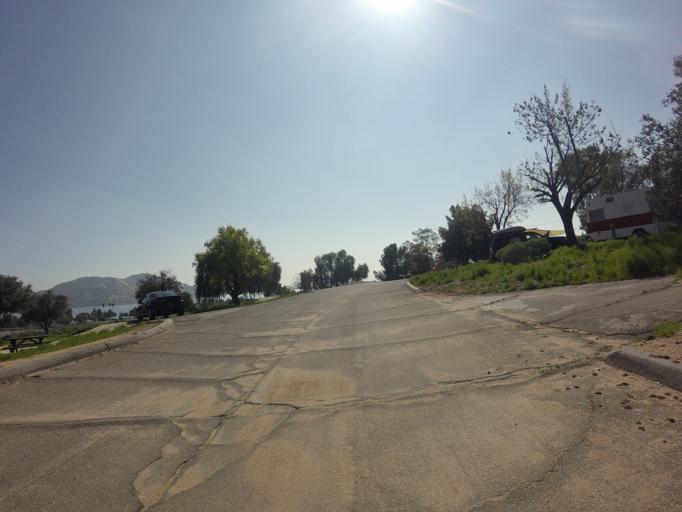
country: US
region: California
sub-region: Riverside County
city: Lakeview
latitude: 33.8725
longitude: -117.1793
